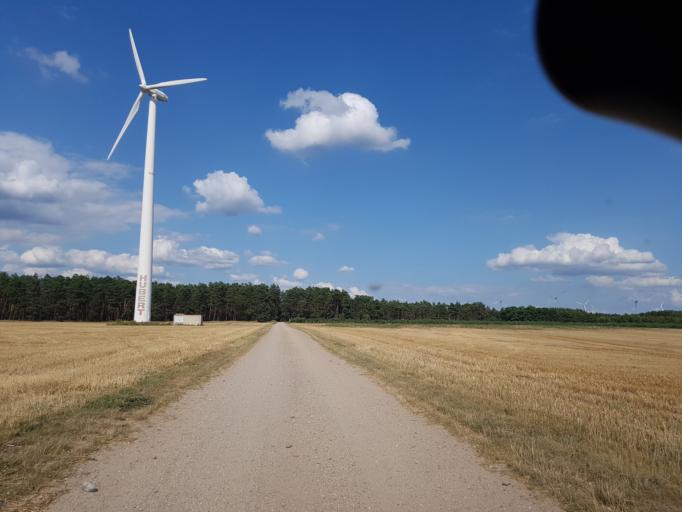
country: DE
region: Brandenburg
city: Finsterwalde
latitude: 51.6356
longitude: 13.7706
